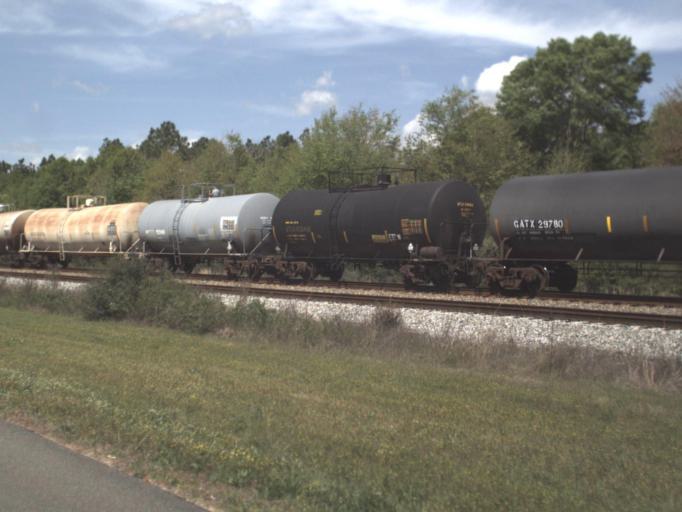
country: US
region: Florida
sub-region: Santa Rosa County
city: East Milton
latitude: 30.6744
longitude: -86.8570
